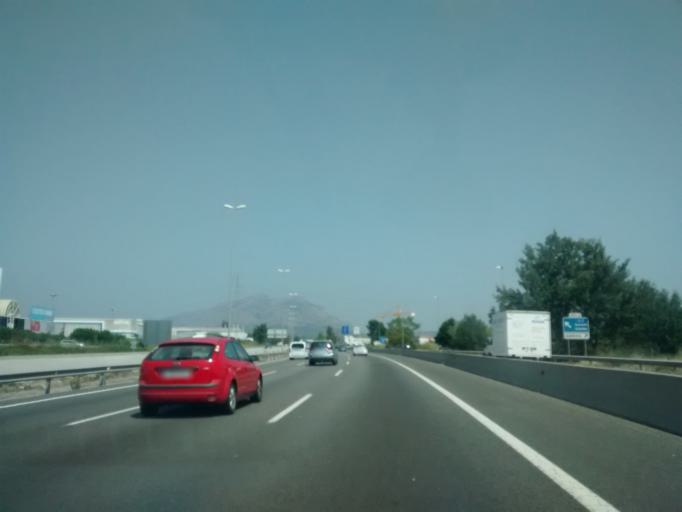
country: ES
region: Catalonia
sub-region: Provincia de Barcelona
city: Abrera
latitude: 41.5062
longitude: 1.9053
